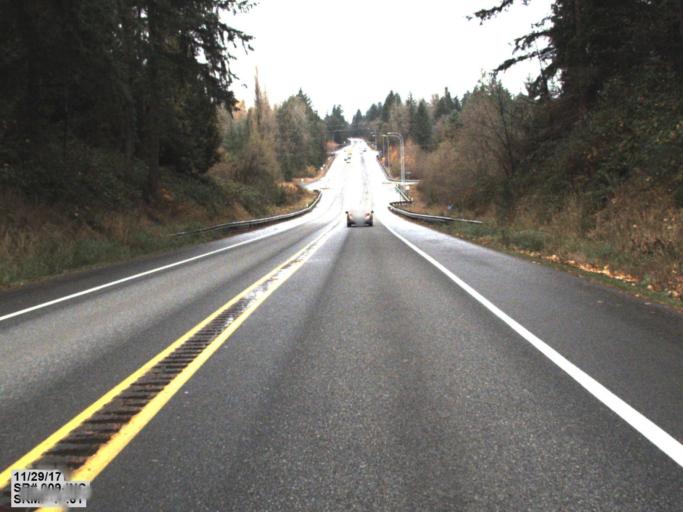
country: US
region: Washington
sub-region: Snohomish County
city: West Lake Stevens
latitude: 47.9720
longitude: -122.1024
